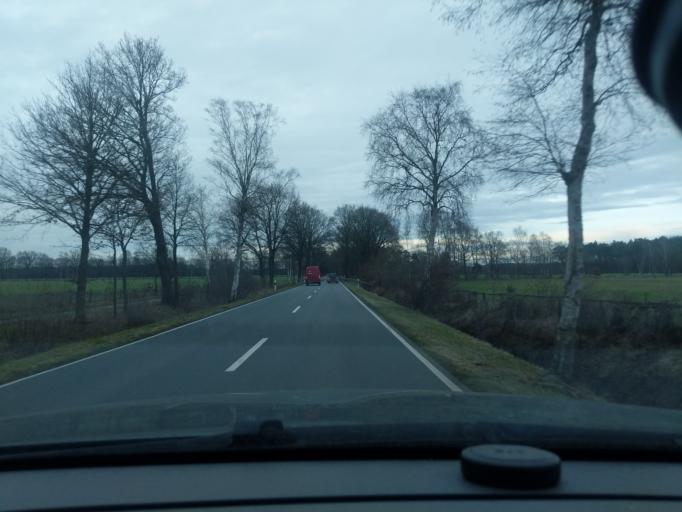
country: DE
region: Lower Saxony
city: Helvesiek
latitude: 53.2326
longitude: 9.4846
